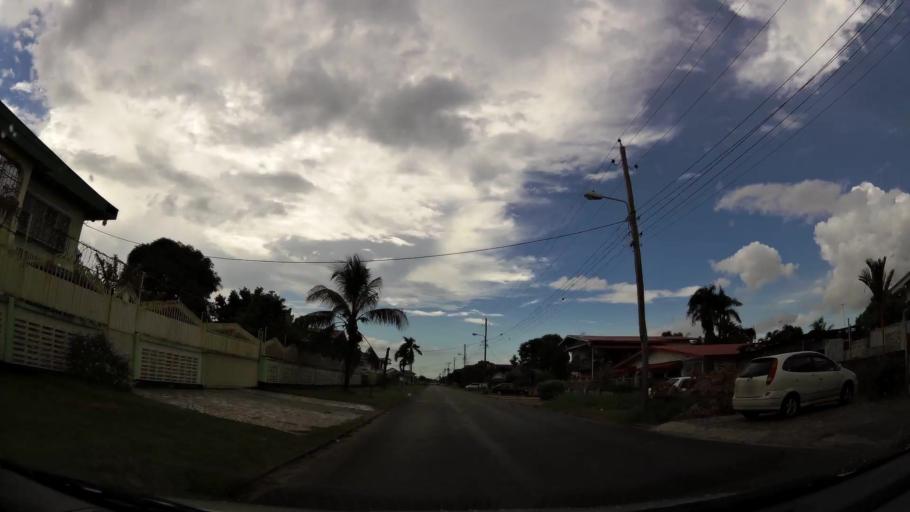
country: SR
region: Paramaribo
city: Paramaribo
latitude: 5.8446
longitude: -55.1273
